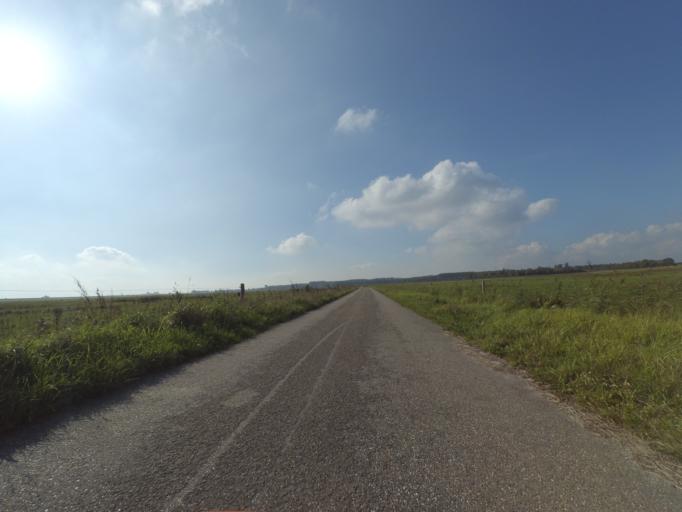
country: NL
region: Flevoland
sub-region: Gemeente Dronten
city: Biddinghuizen
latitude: 52.4033
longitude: 5.6572
